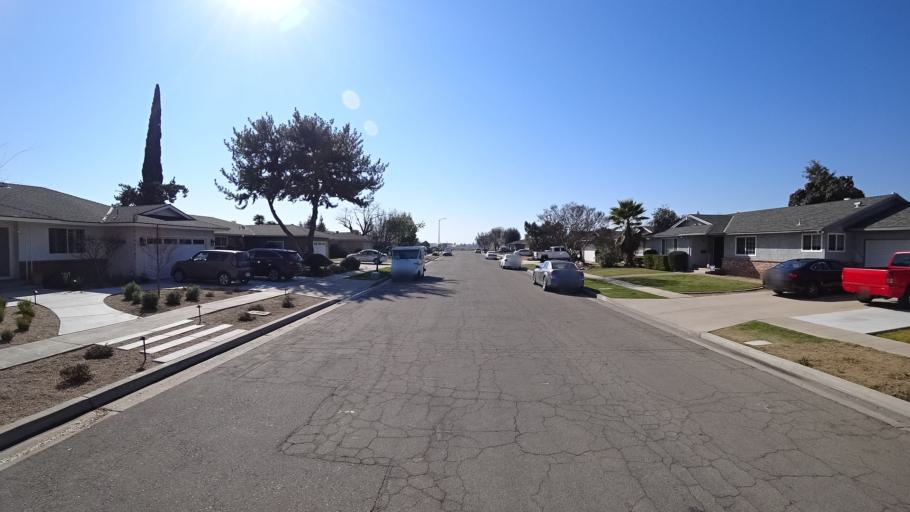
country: US
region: California
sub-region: Fresno County
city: Clovis
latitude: 36.8316
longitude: -119.7413
